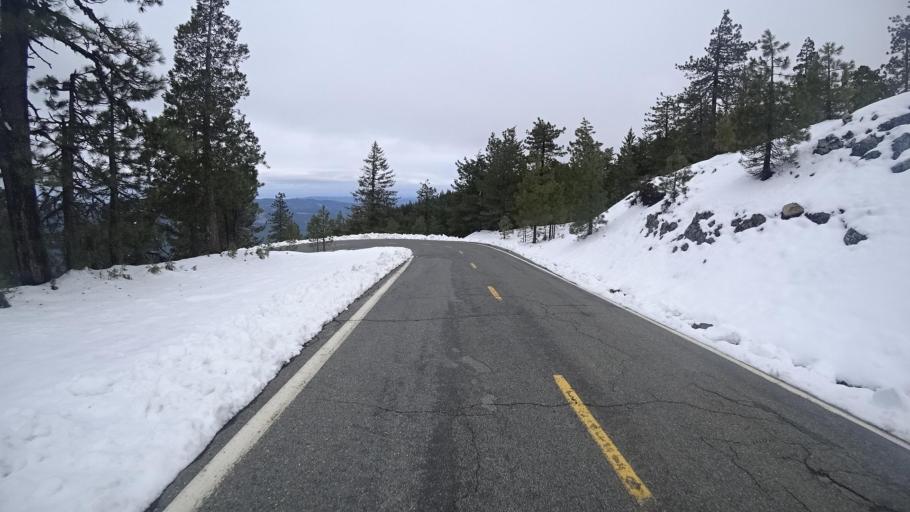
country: US
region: California
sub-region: Humboldt County
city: Willow Creek
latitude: 40.8672
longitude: -123.7373
